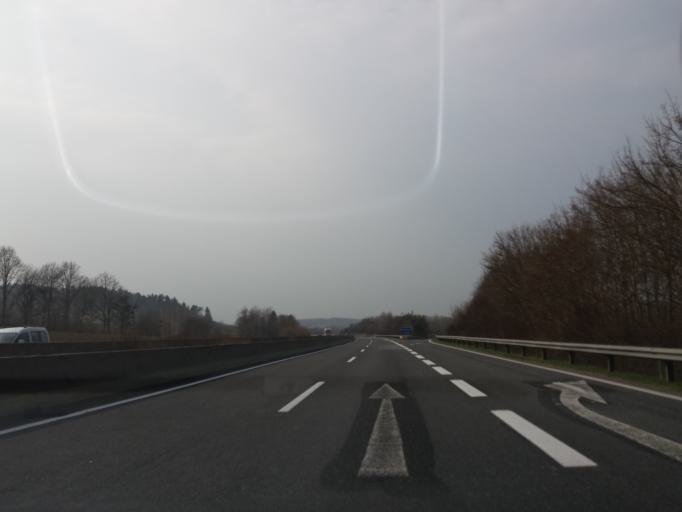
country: AT
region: Styria
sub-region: Politischer Bezirk Weiz
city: Sinabelkirchen
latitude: 47.0970
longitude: 15.8225
